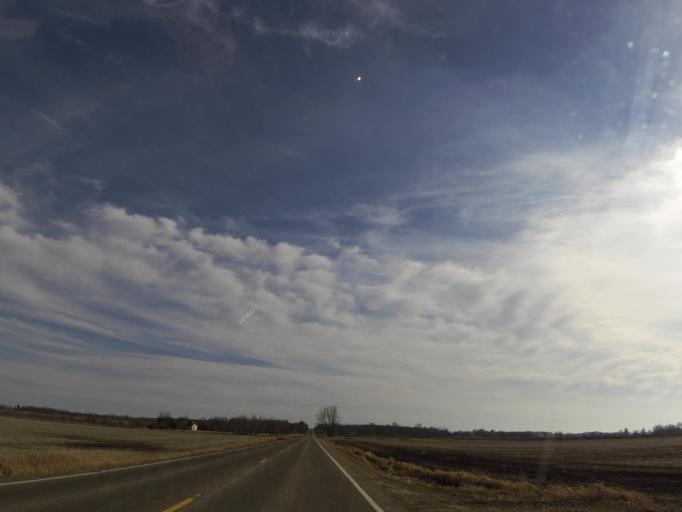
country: US
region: Minnesota
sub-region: Rice County
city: Northfield
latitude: 44.5005
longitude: -93.2003
